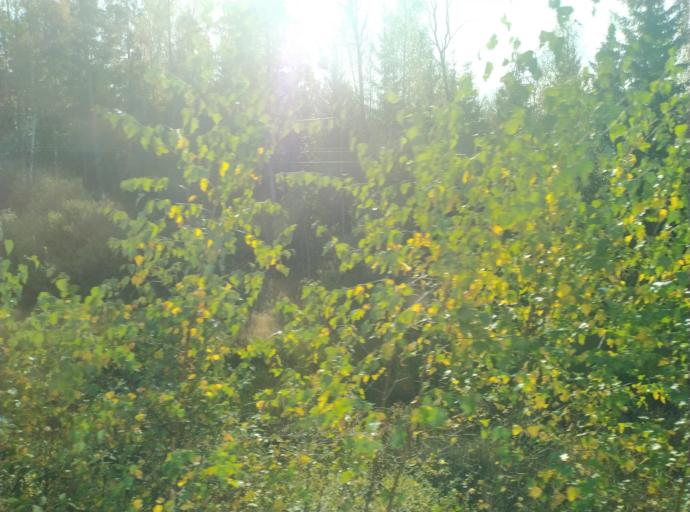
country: RU
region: Moskovskaya
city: Novo-Nikol'skoye
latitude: 56.5452
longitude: 37.5540
